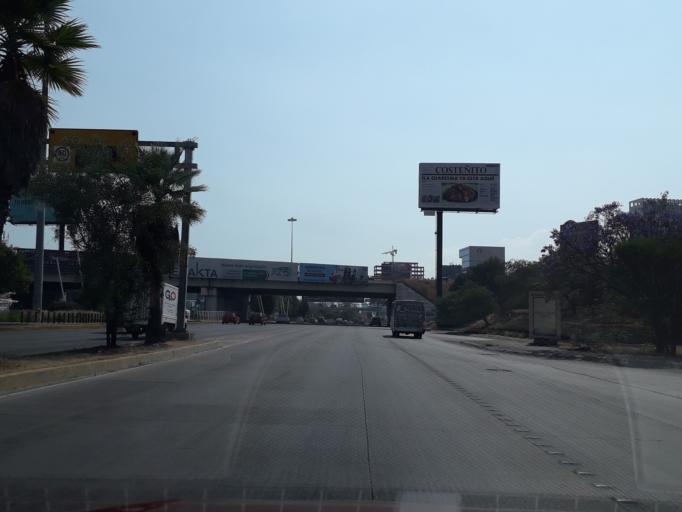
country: MX
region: Puebla
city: Puebla
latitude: 19.0296
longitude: -98.2316
